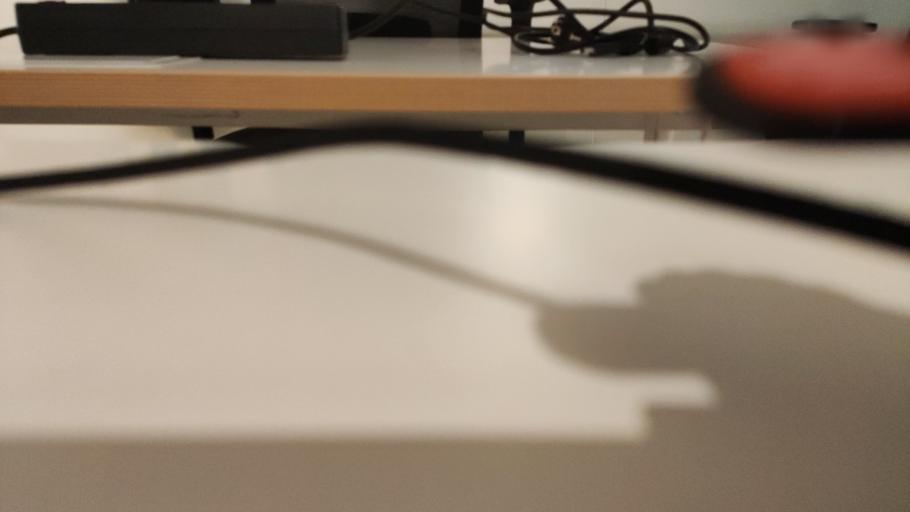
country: RU
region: Moskovskaya
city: Proletarskiy
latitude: 54.9861
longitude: 37.3179
